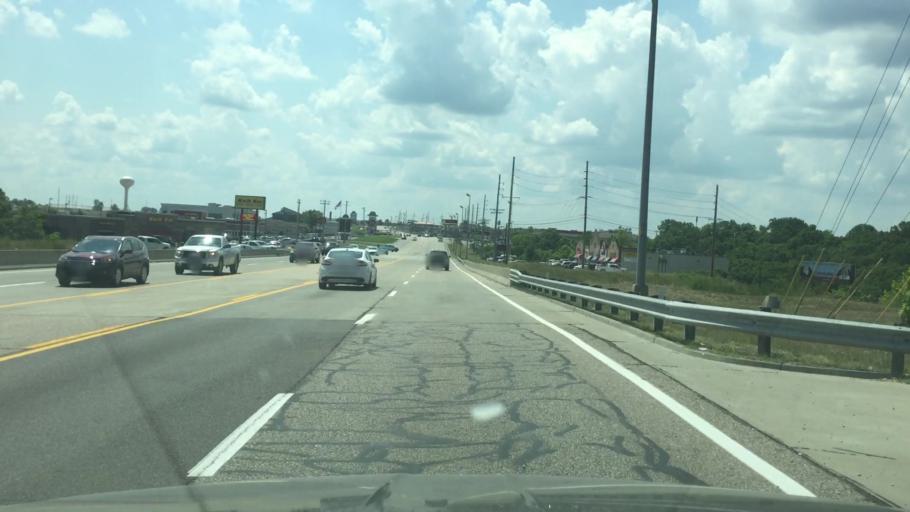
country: US
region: Missouri
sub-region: Miller County
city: Lake Ozark
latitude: 38.1660
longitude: -92.6105
